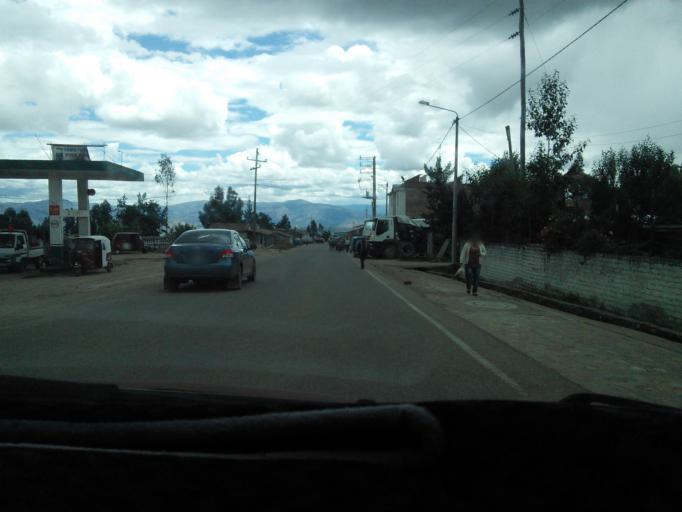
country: PE
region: Ayacucho
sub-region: Provincia de Huamanga
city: Quinua
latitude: -13.0498
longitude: -74.1368
